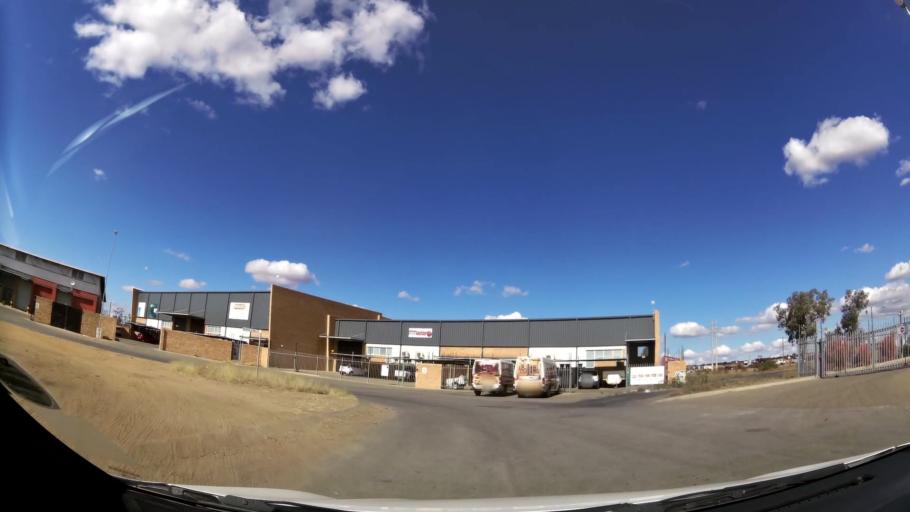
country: ZA
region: Limpopo
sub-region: Capricorn District Municipality
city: Polokwane
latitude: -23.8689
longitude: 29.4827
